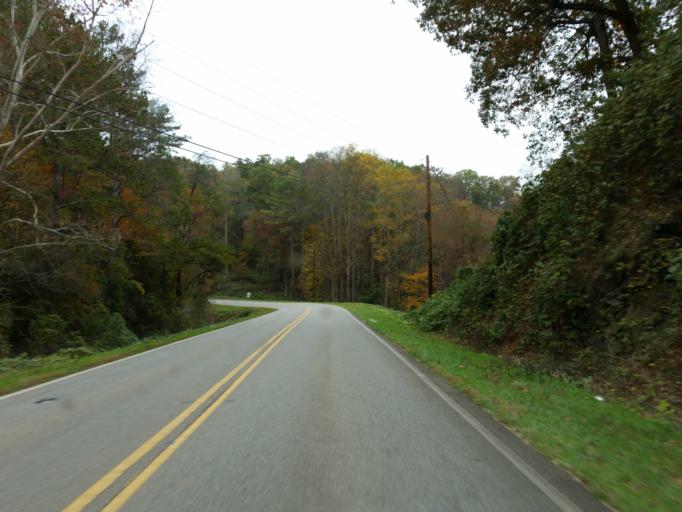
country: US
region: Georgia
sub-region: Pickens County
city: Jasper
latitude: 34.4834
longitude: -84.4218
